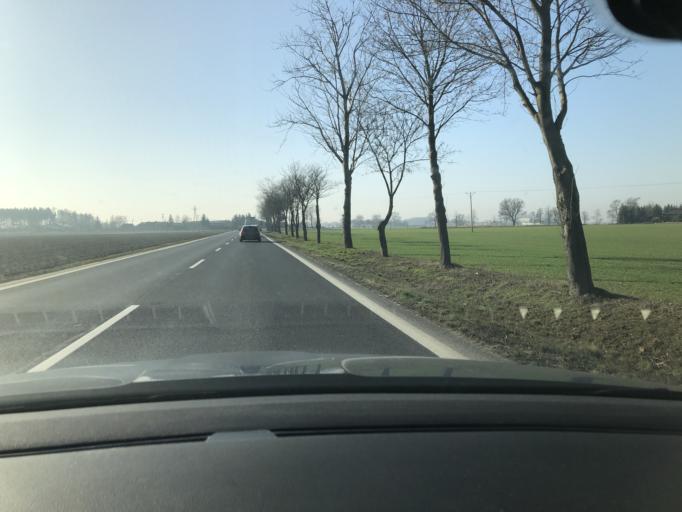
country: PL
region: Greater Poland Voivodeship
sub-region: Powiat poznanski
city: Buk
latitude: 52.3726
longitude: 16.5544
